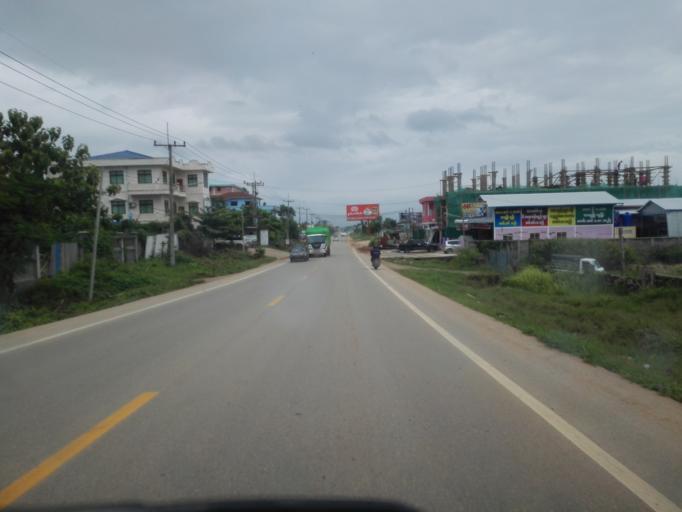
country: TH
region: Tak
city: Mae Sot
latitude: 16.6854
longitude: 98.4828
